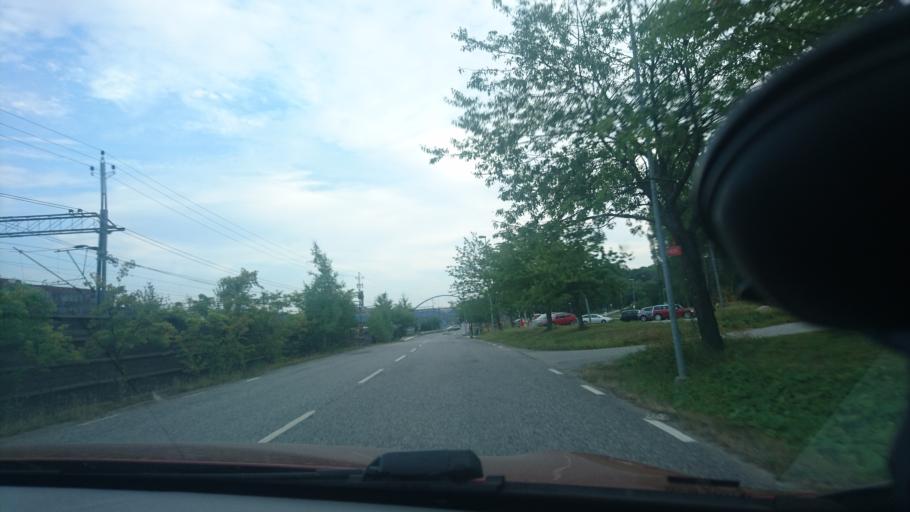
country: SE
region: Stockholm
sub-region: Upplands Vasby Kommun
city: Upplands Vaesby
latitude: 59.5229
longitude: 17.8995
